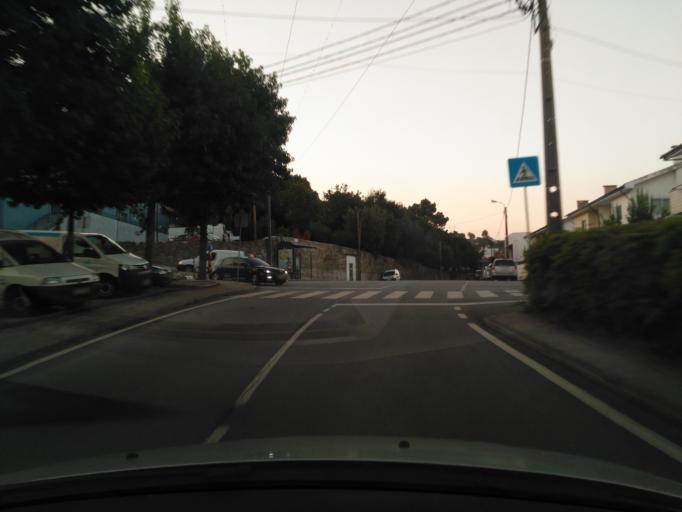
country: PT
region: Braga
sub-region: Braga
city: Adaufe
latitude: 41.5641
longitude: -8.3927
